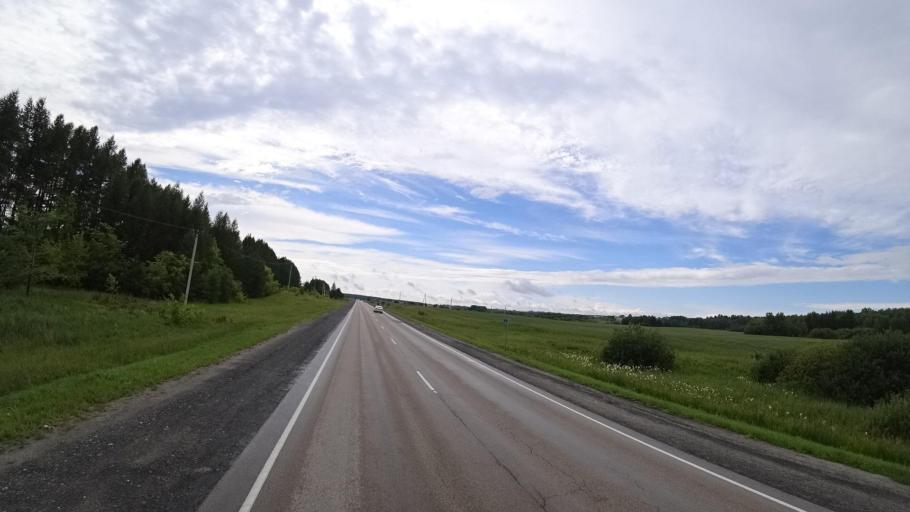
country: RU
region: Sverdlovsk
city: Kamyshlov
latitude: 56.8441
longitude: 62.8118
